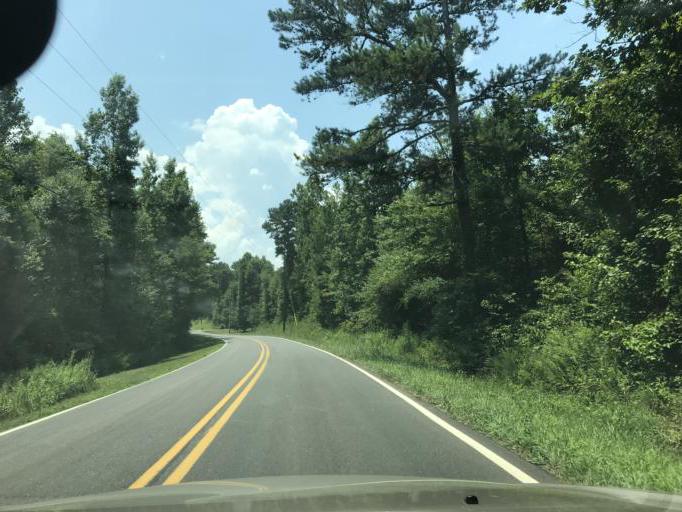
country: US
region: Georgia
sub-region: Dawson County
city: Dawsonville
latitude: 34.3269
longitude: -84.1599
